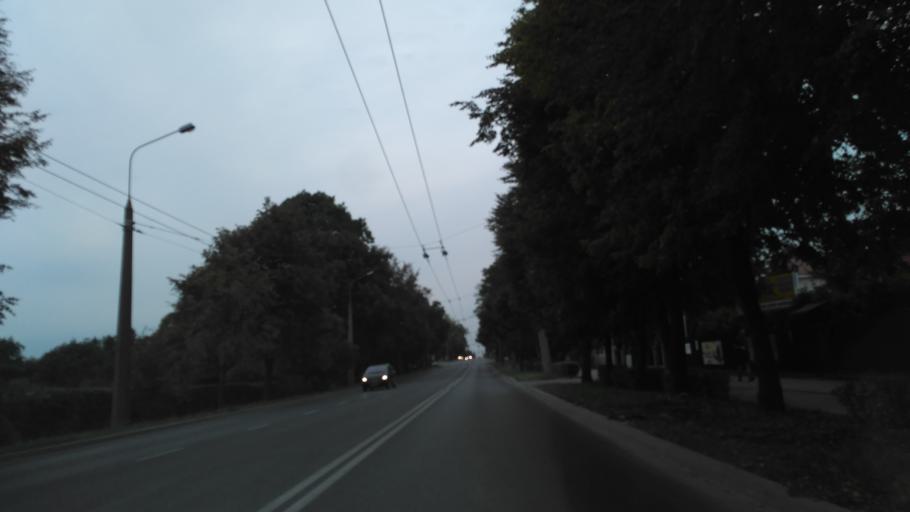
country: PL
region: Lublin Voivodeship
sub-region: Powiat lubelski
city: Lublin
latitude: 51.2281
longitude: 22.6003
